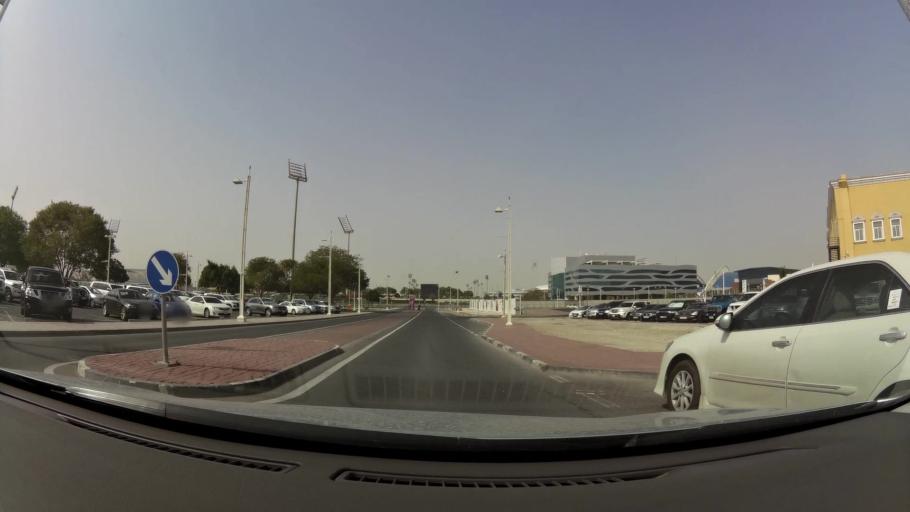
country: QA
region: Baladiyat ar Rayyan
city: Ar Rayyan
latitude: 25.2616
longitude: 51.4402
